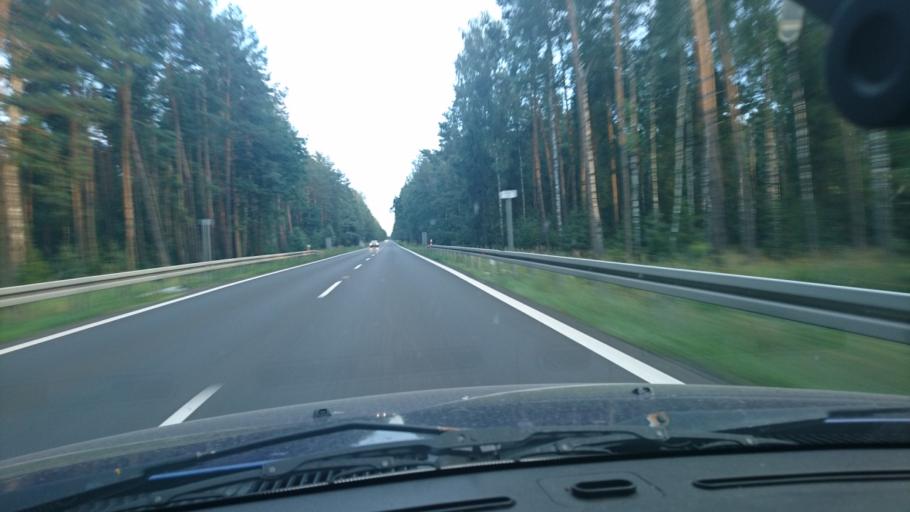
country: PL
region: Silesian Voivodeship
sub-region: Powiat tarnogorski
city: Tworog
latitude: 50.5706
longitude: 18.7108
